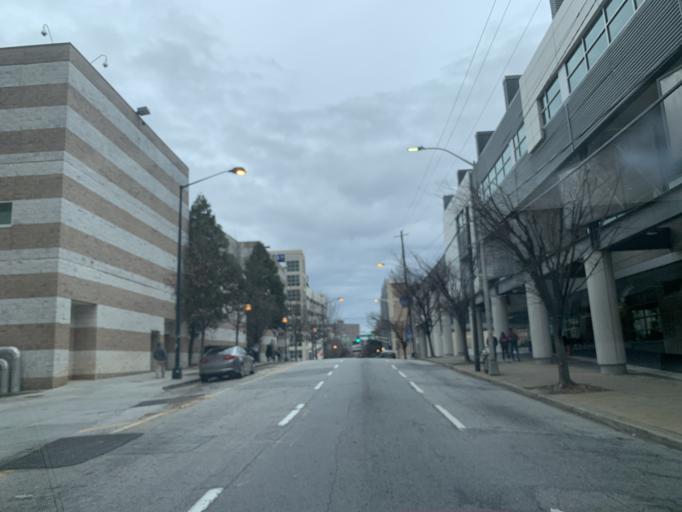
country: US
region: Georgia
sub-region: Fulton County
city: Atlanta
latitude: 33.7520
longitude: -84.3848
